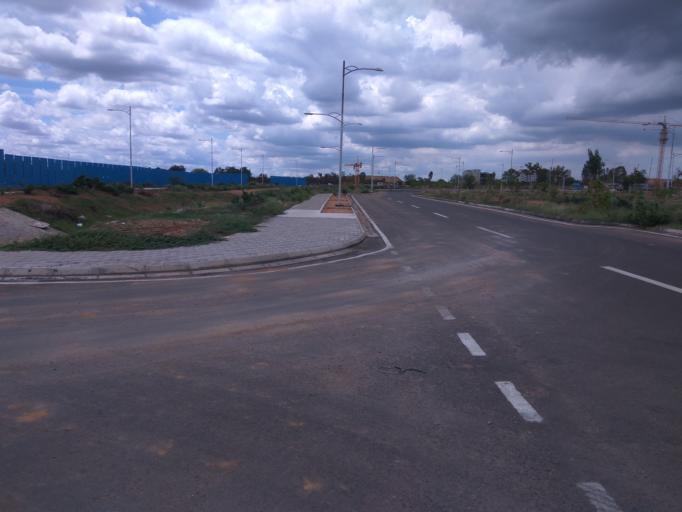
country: IN
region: Telangana
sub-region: Medak
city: Sangareddi
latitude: 17.5861
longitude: 78.1201
